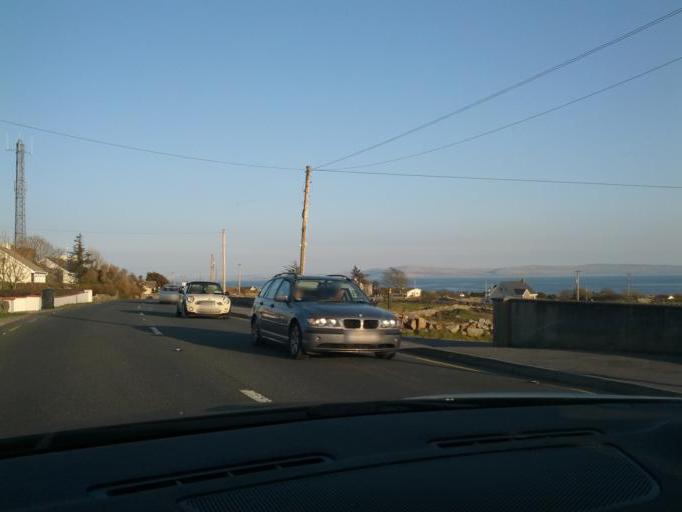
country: IE
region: Connaught
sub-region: County Galway
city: Oughterard
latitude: 53.2409
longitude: -9.4316
